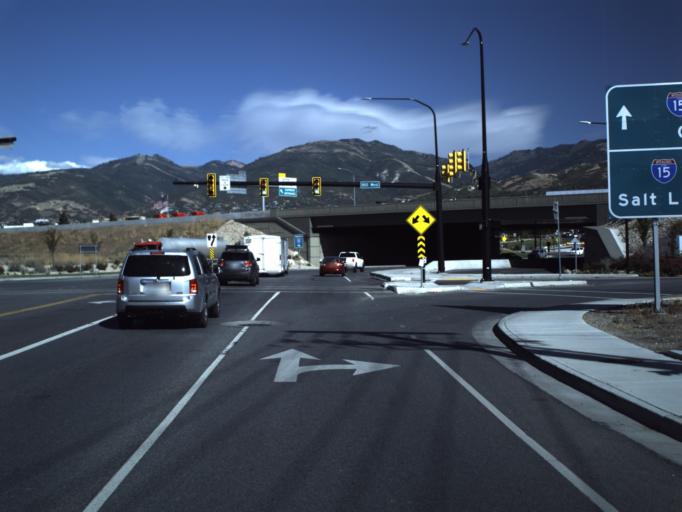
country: US
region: Utah
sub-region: Davis County
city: North Salt Lake
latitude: 40.8616
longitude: -111.9037
